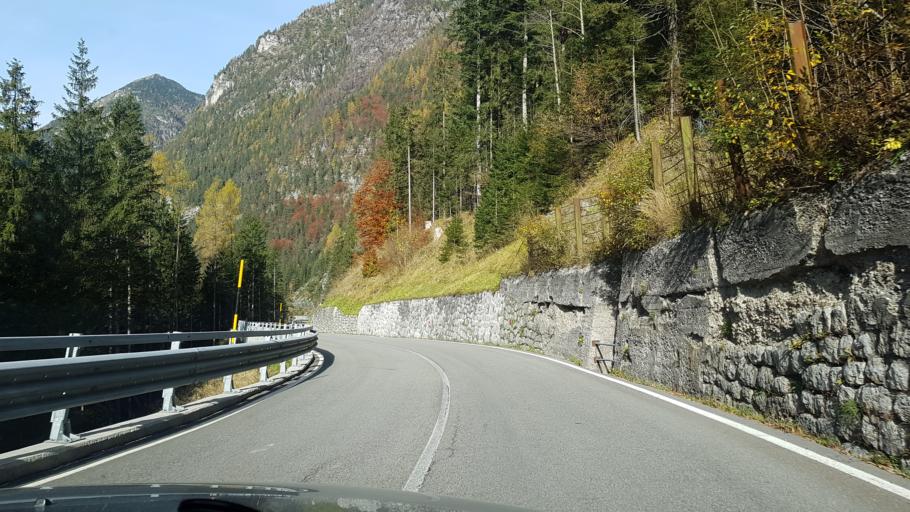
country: IT
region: Veneto
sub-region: Provincia di Belluno
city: Sappada
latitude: 46.5729
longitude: 12.6496
